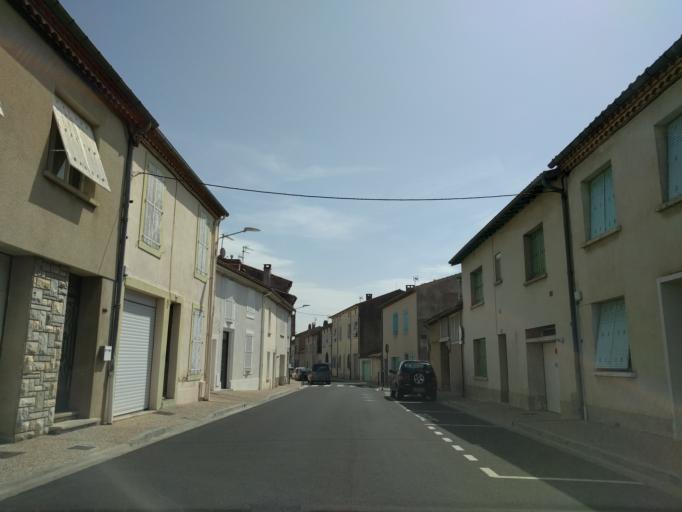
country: FR
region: Midi-Pyrenees
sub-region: Departement du Tarn
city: Castres
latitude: 43.6093
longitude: 2.2319
